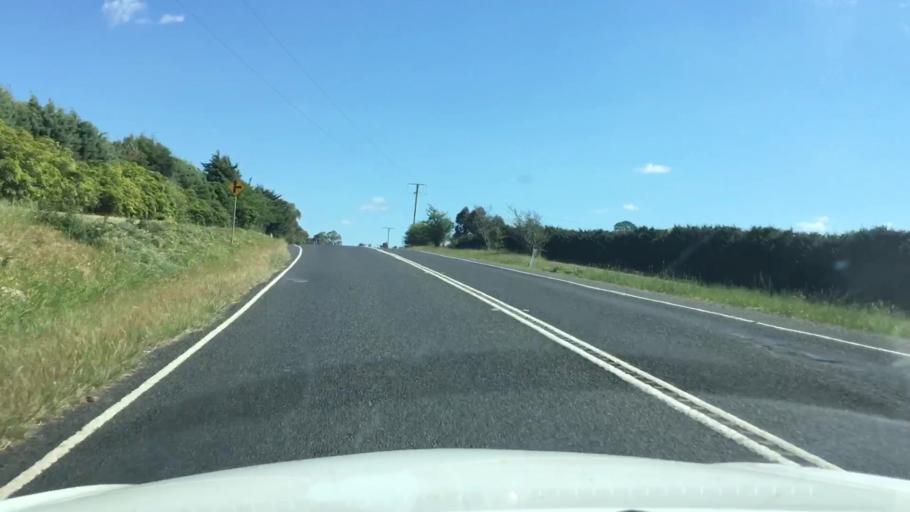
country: AU
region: Victoria
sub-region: Nillumbik
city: North Warrandyte
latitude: -37.6851
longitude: 145.2353
